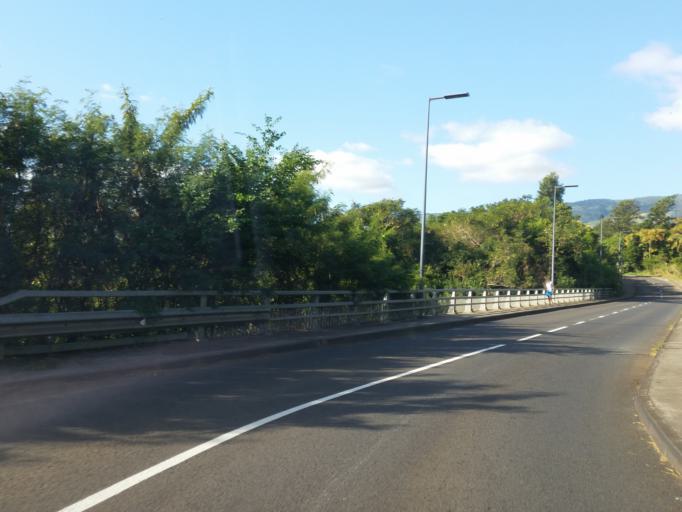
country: RE
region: Reunion
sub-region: Reunion
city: Sainte-Marie
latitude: -20.9104
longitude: 55.5017
